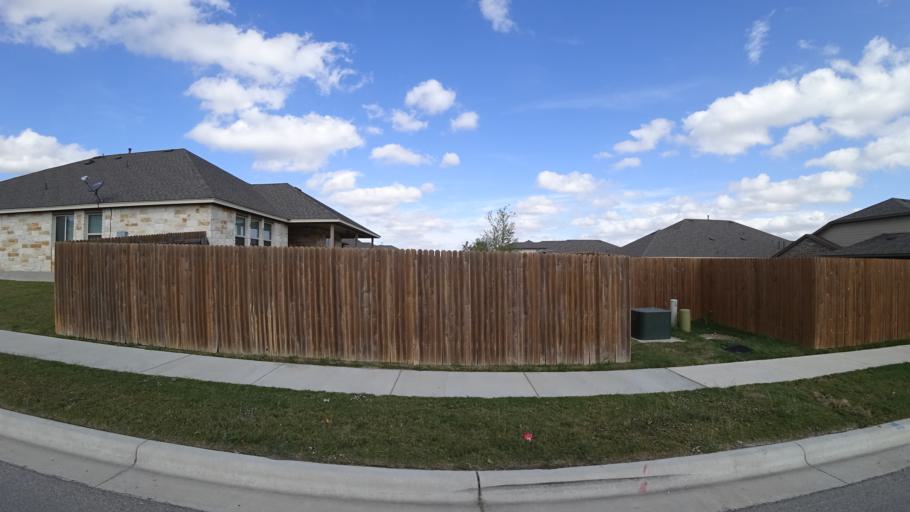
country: US
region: Texas
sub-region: Travis County
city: Windemere
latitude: 30.4777
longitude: -97.6549
